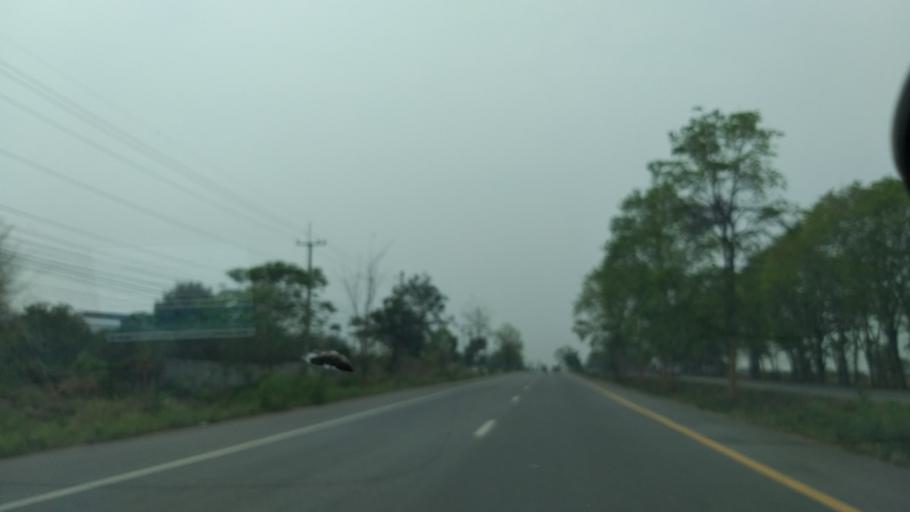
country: TH
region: Chachoengsao
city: Plaeng Yao
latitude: 13.5029
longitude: 101.2707
